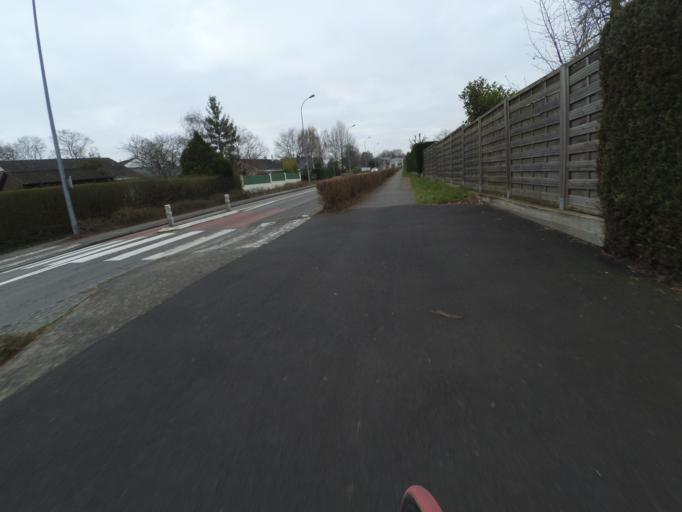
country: FR
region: Pays de la Loire
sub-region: Departement de la Loire-Atlantique
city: Carquefou
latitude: 47.2798
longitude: -1.4853
